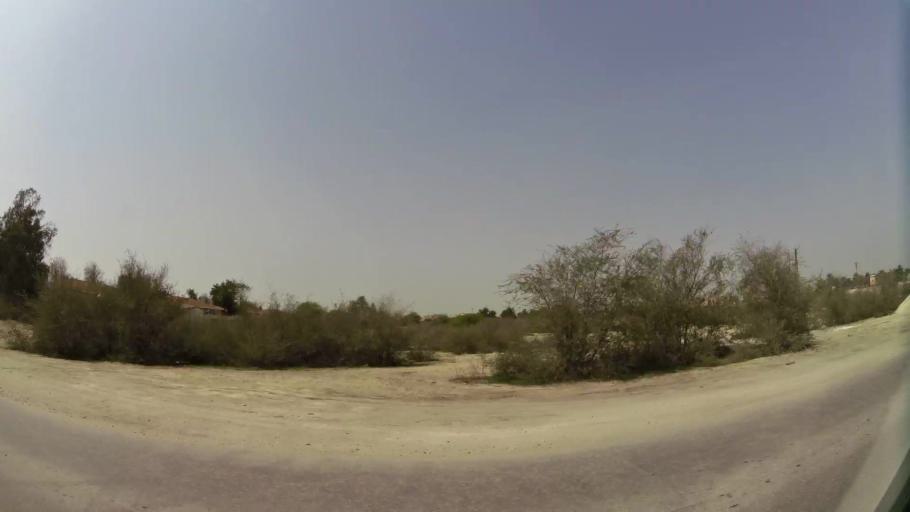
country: BH
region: Manama
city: Jidd Hafs
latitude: 26.2208
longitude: 50.4782
